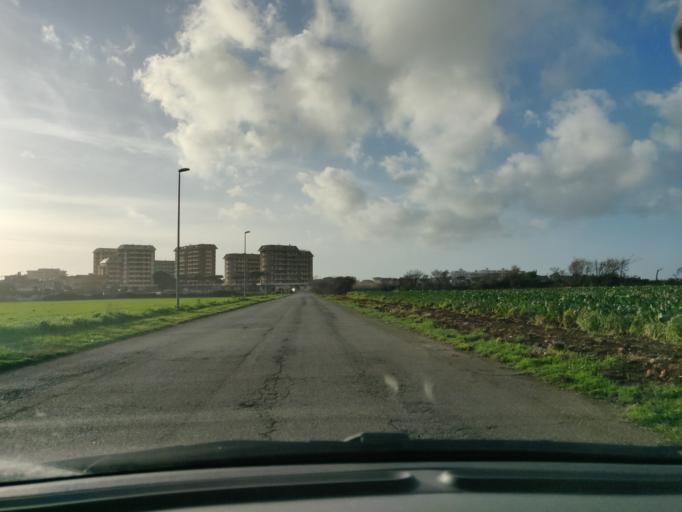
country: IT
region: Latium
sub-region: Provincia di Viterbo
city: Tarquinia
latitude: 42.2249
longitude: 11.7130
